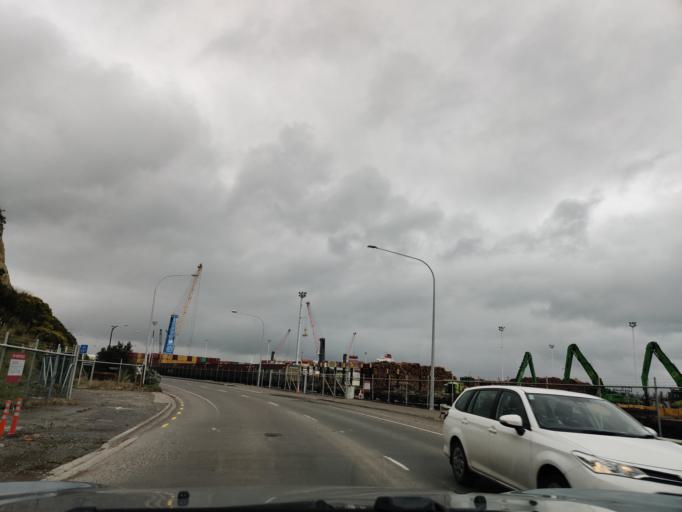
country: NZ
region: Hawke's Bay
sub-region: Napier City
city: Napier
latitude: -39.4788
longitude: 176.9200
